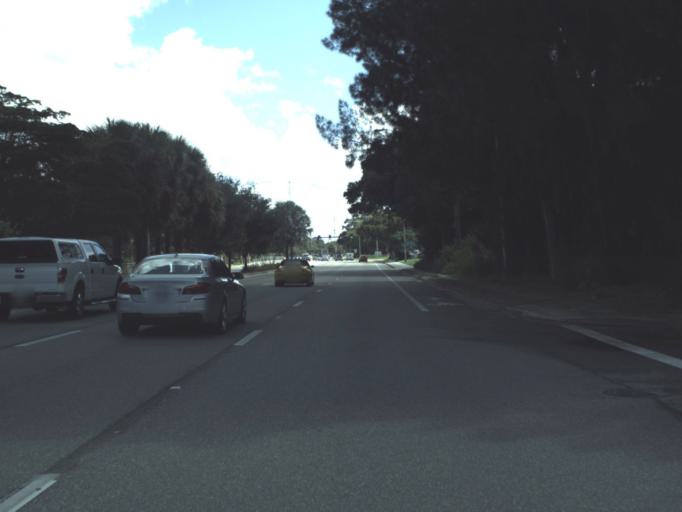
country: US
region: Florida
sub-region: Sarasota County
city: Kensington Park
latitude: 27.3375
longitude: -82.4835
